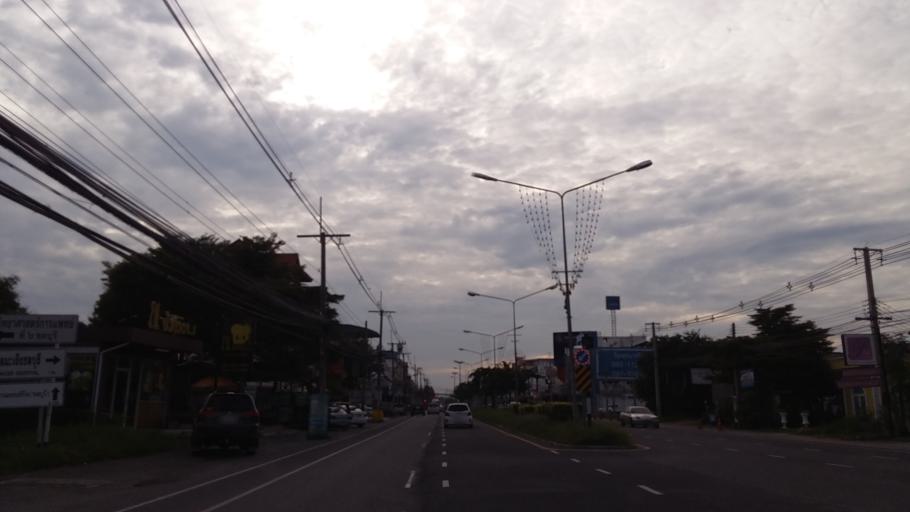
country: TH
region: Chon Buri
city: Chon Buri
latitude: 13.3384
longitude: 100.9535
